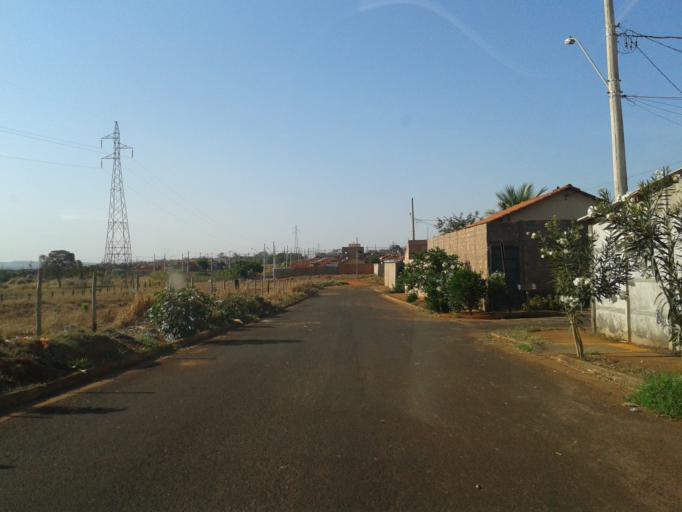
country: BR
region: Minas Gerais
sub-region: Ituiutaba
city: Ituiutaba
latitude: -18.9832
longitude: -49.4282
